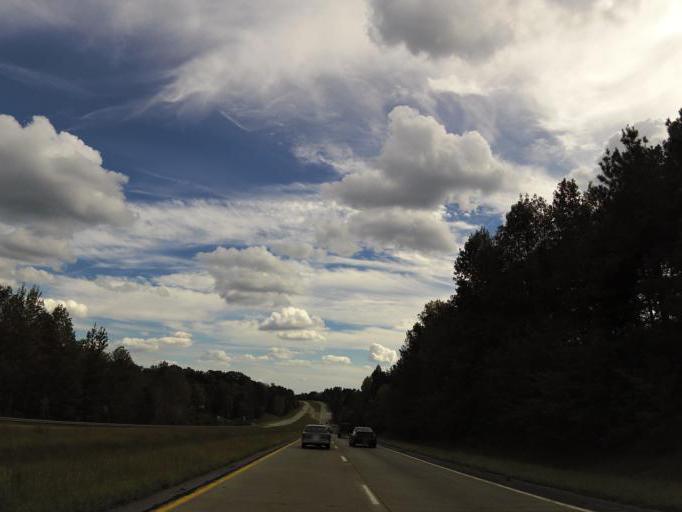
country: US
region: Georgia
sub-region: Pickens County
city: Jasper
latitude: 34.4203
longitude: -84.4302
